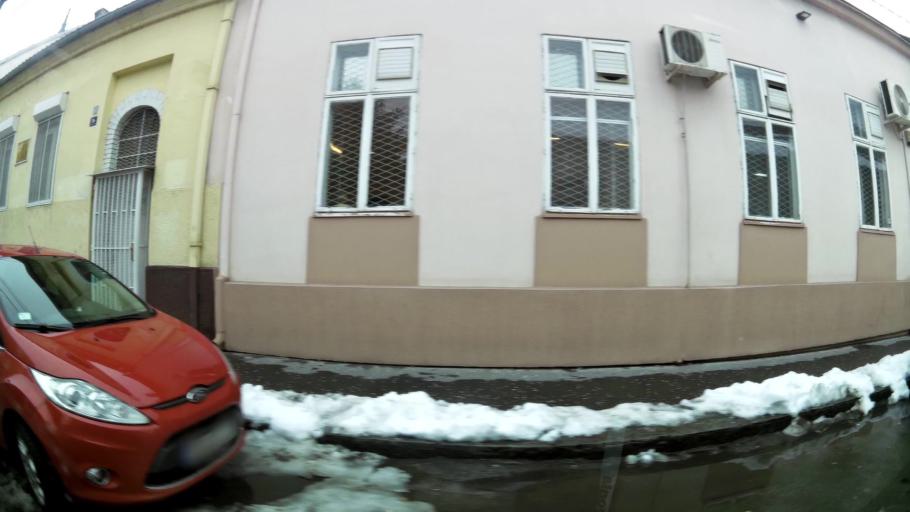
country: RS
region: Central Serbia
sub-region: Belgrade
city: Zemun
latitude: 44.8440
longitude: 20.4095
